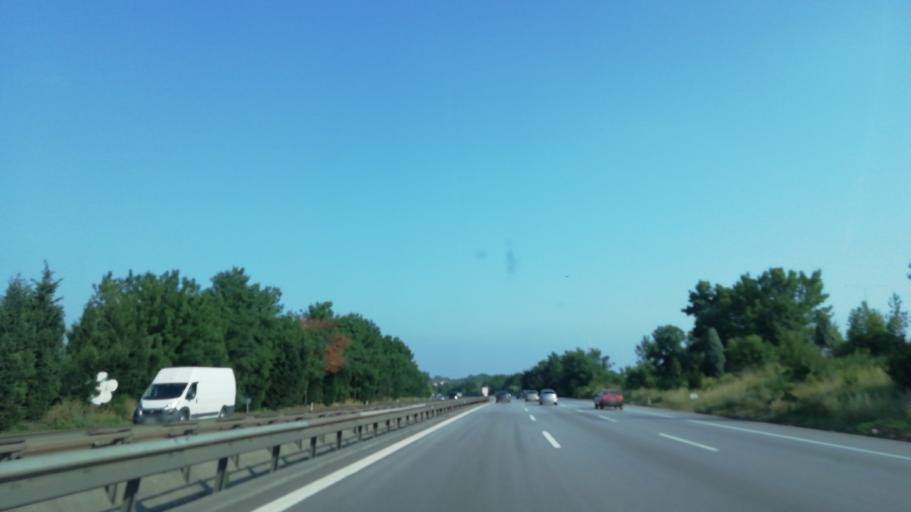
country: TR
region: Kocaeli
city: Derbent
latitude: 40.7187
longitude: 30.1103
